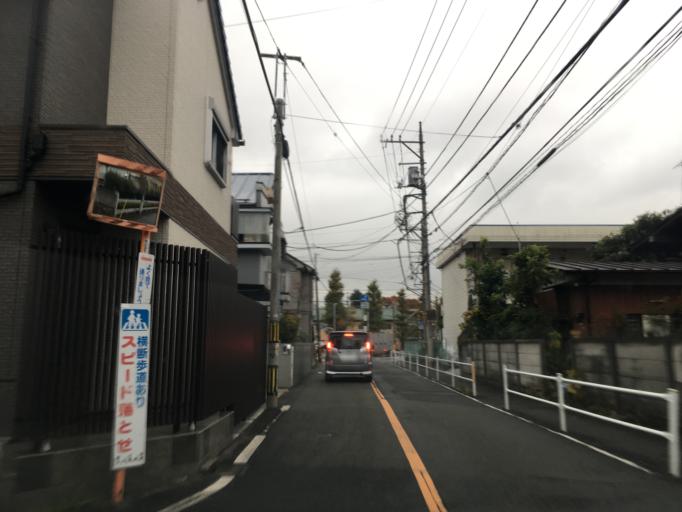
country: JP
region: Tokyo
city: Kokubunji
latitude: 35.6884
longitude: 139.4414
